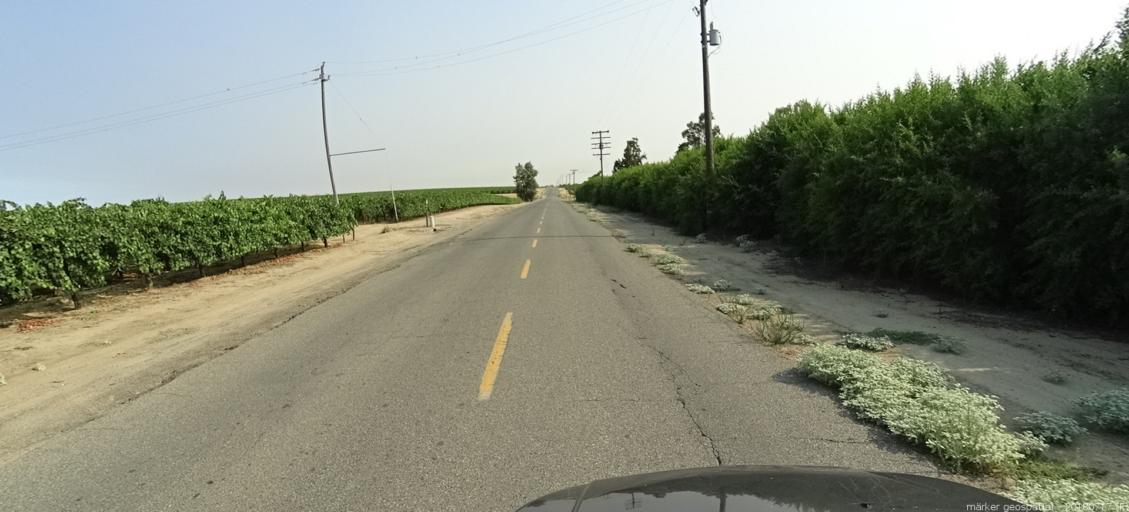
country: US
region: California
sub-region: Madera County
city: Madera Acres
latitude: 37.0589
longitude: -120.1108
